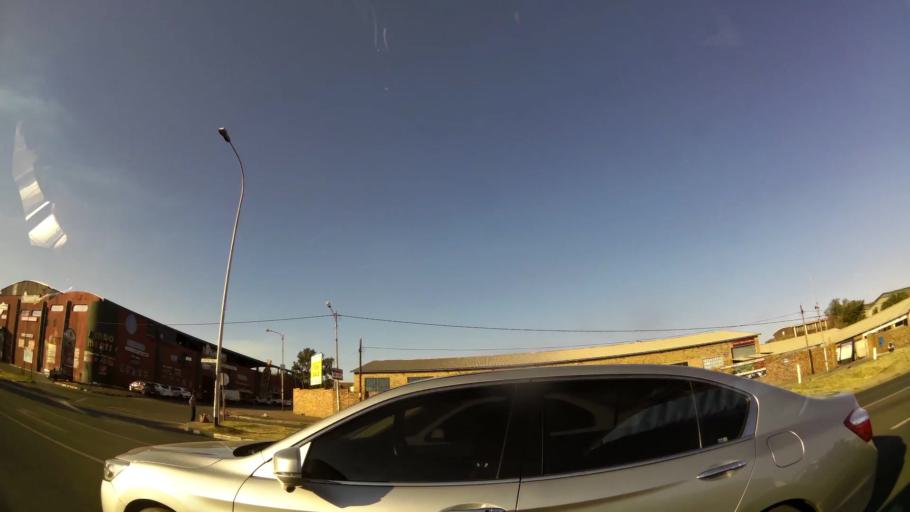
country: ZA
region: Gauteng
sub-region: City of Johannesburg Metropolitan Municipality
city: Roodepoort
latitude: -26.1477
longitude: 27.8629
